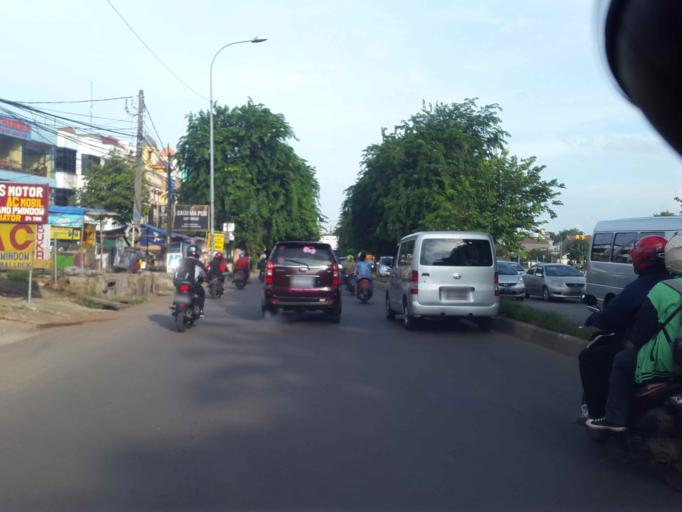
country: ID
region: West Java
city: Bekasi
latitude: -6.2492
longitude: 106.9634
